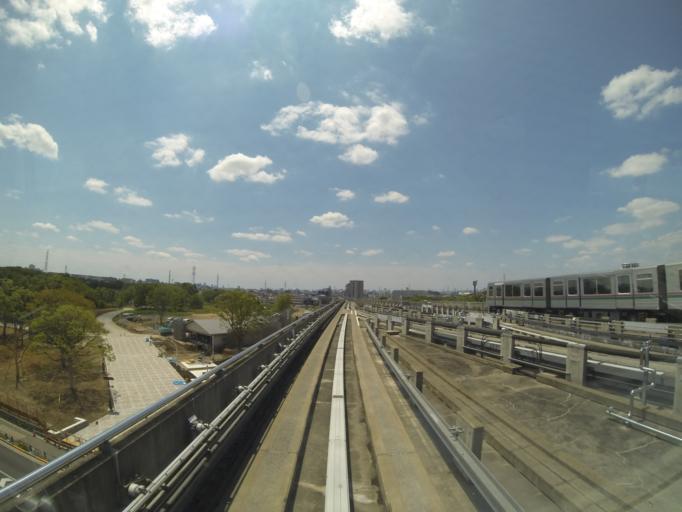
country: JP
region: Saitama
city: Soka
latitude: 35.7960
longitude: 139.7703
